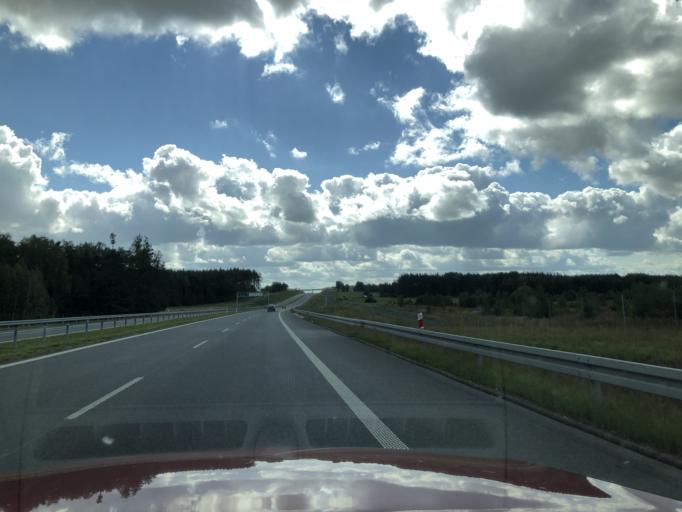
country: PL
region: West Pomeranian Voivodeship
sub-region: Powiat szczecinecki
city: Szczecinek
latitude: 53.6779
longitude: 16.7366
